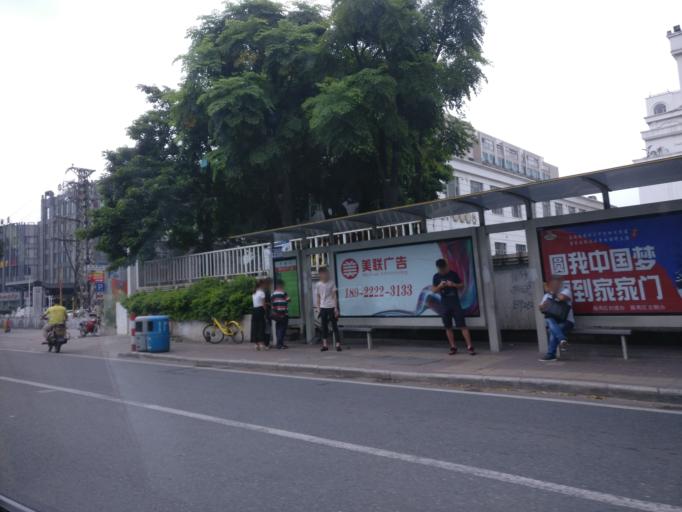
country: CN
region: Guangdong
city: Dashi
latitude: 23.0382
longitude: 113.3229
